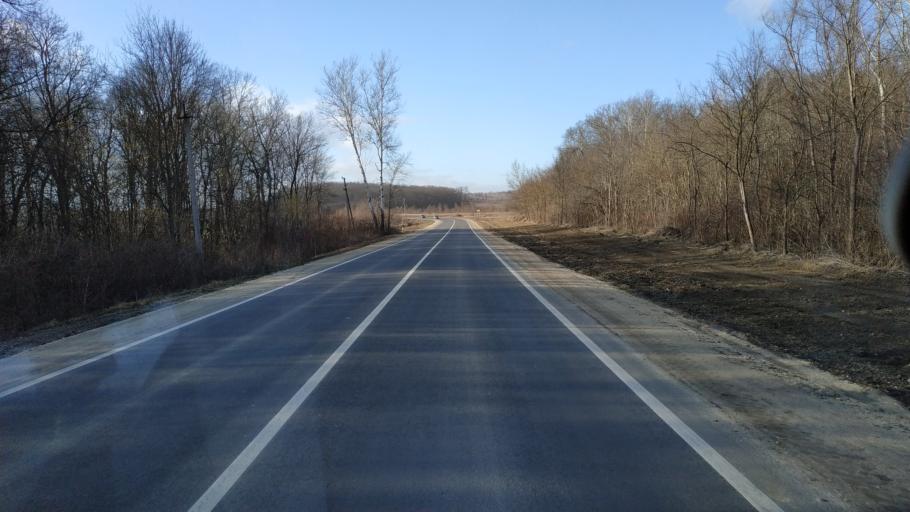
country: MD
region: Calarasi
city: Calarasi
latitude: 47.3039
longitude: 28.1379
